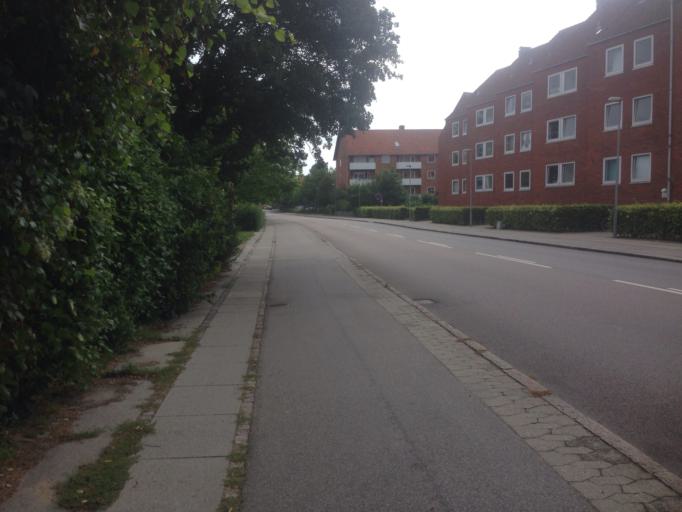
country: DK
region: Capital Region
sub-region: Ballerup Kommune
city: Ballerup
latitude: 55.7330
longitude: 12.3552
